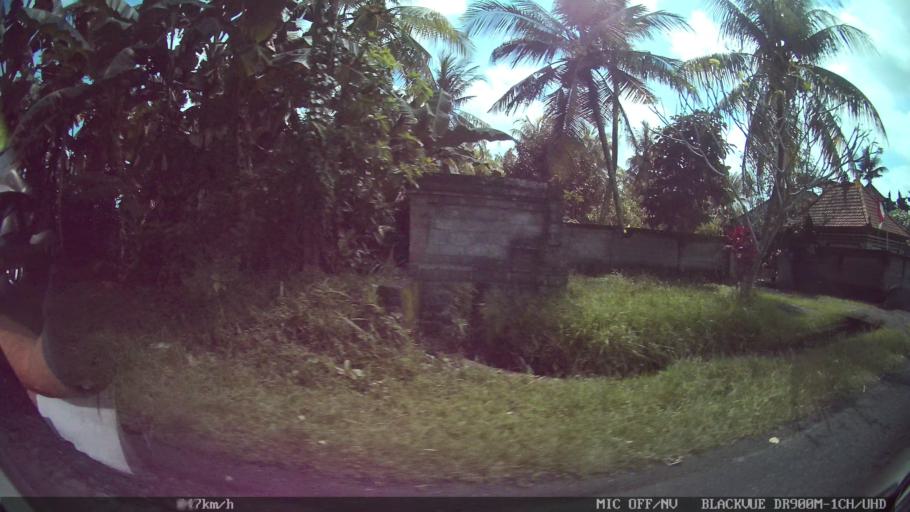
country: ID
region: Bali
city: Banjar Apuan Kaja
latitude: -8.5196
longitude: 115.3296
